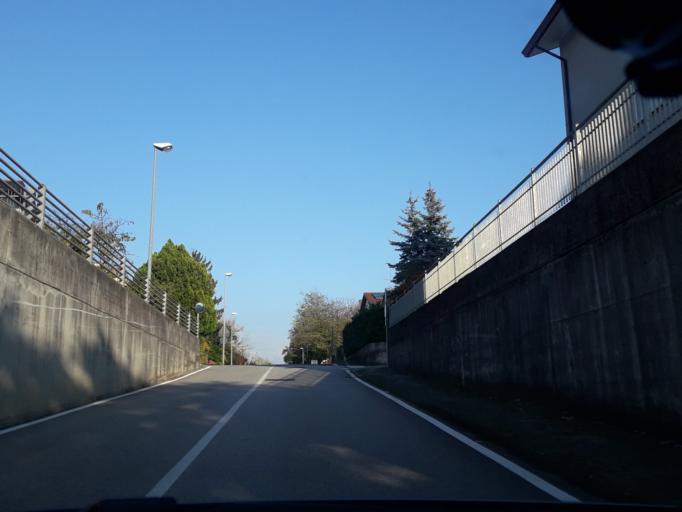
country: IT
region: Friuli Venezia Giulia
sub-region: Provincia di Udine
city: Pradamano
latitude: 46.0298
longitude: 13.2927
